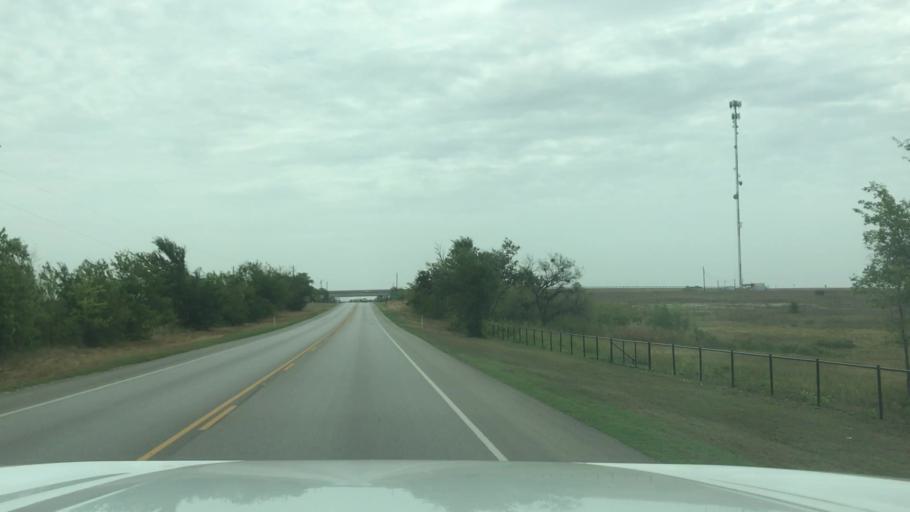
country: US
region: Texas
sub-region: Erath County
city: Dublin
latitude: 32.0947
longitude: -98.3733
